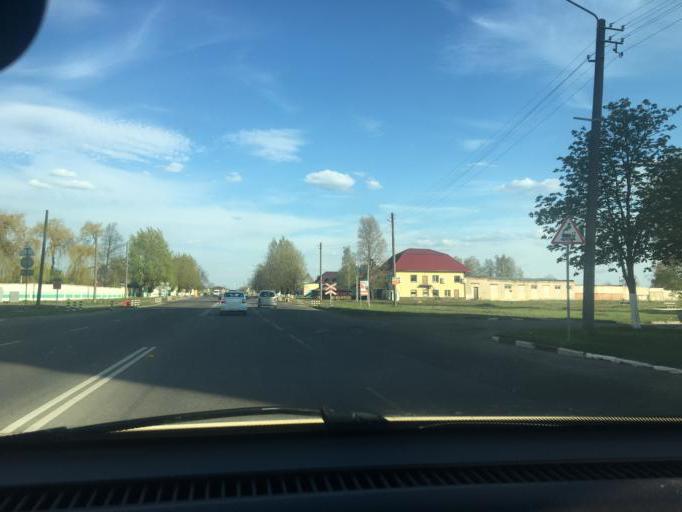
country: BY
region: Mogilev
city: Babruysk
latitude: 53.1502
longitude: 29.1881
